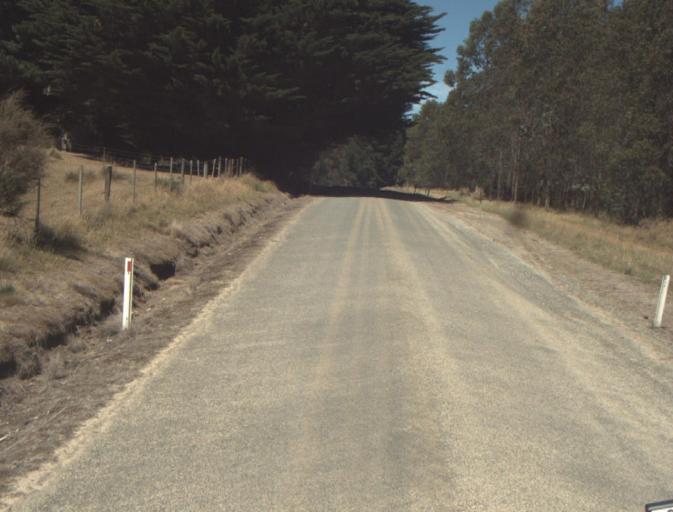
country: AU
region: Tasmania
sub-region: Dorset
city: Scottsdale
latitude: -41.3257
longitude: 147.4764
